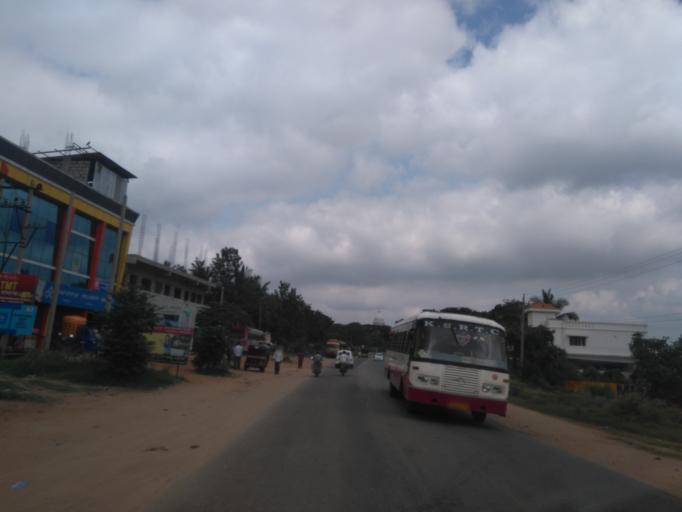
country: IN
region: Karnataka
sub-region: Mysore
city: Mysore
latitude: 12.2989
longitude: 76.6972
